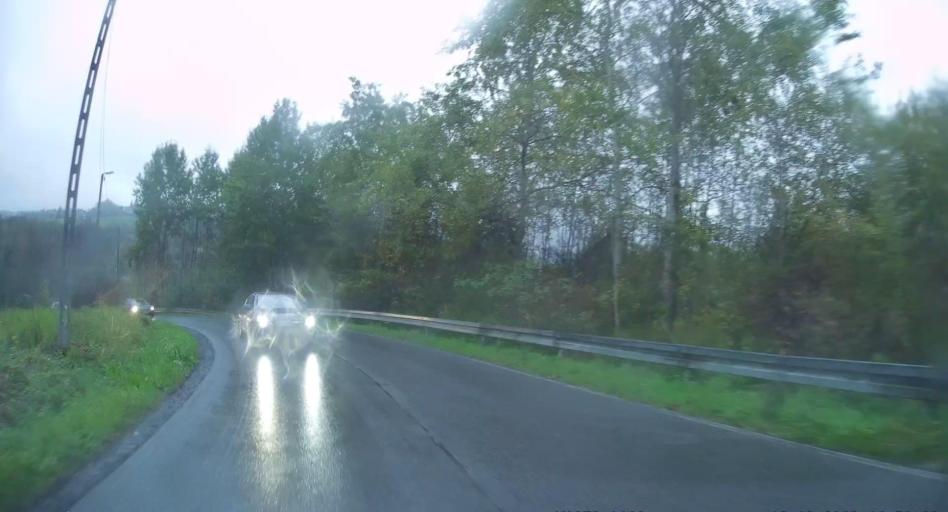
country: PL
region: Lesser Poland Voivodeship
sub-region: Powiat krakowski
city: Ochojno
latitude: 49.9626
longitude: 20.0022
